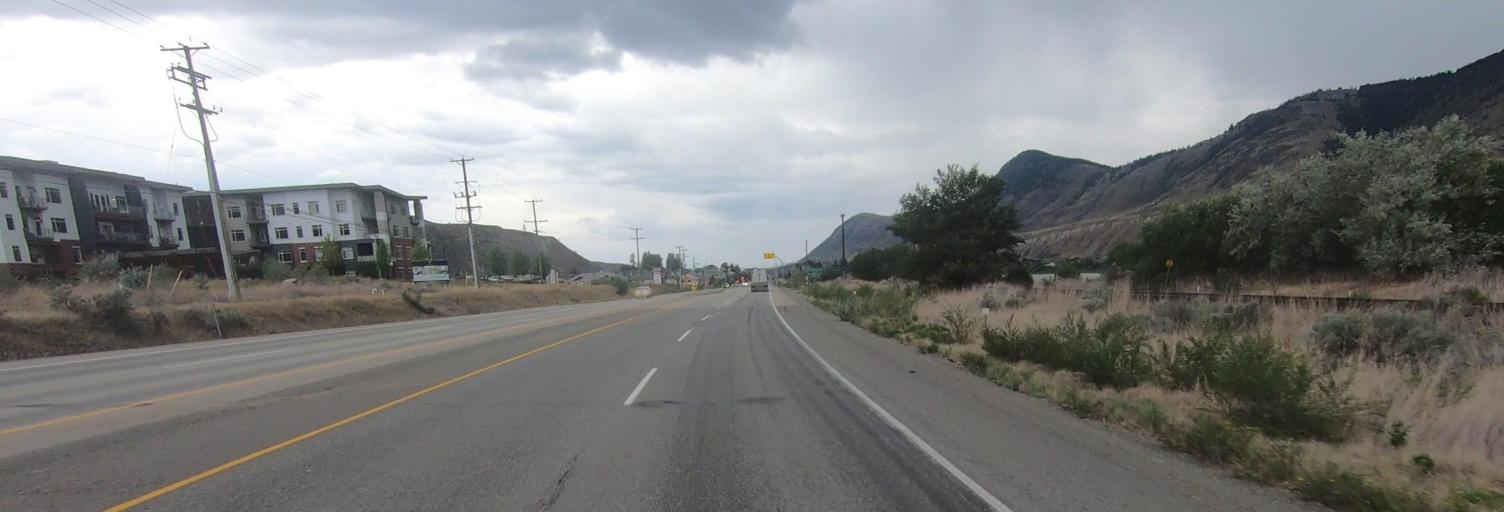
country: CA
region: British Columbia
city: Kamloops
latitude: 50.6712
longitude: -120.2222
